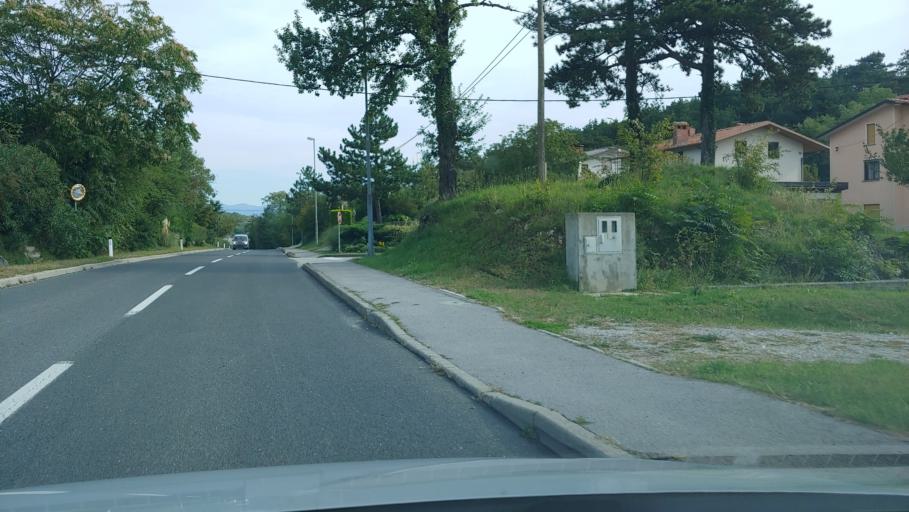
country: SI
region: Nova Gorica
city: Sempas
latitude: 45.9096
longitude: 13.7705
